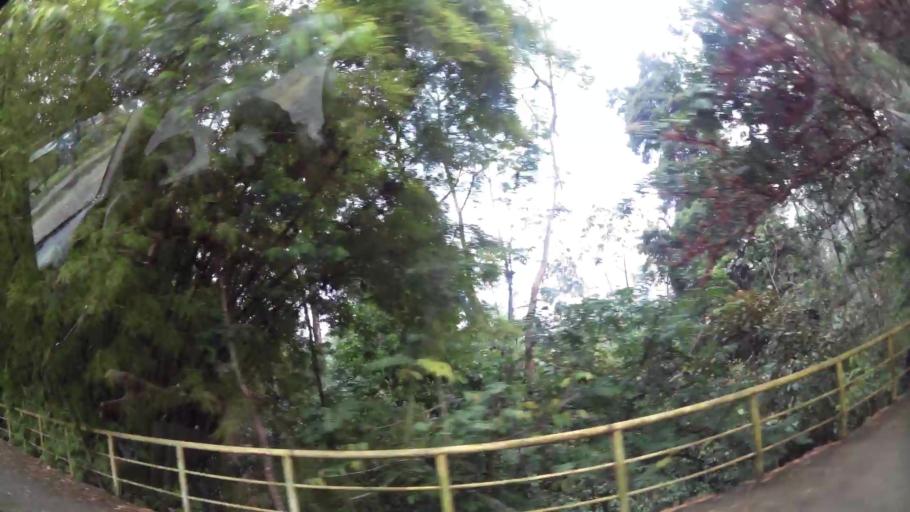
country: CO
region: Antioquia
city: Medellin
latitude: 6.2073
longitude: -75.5523
